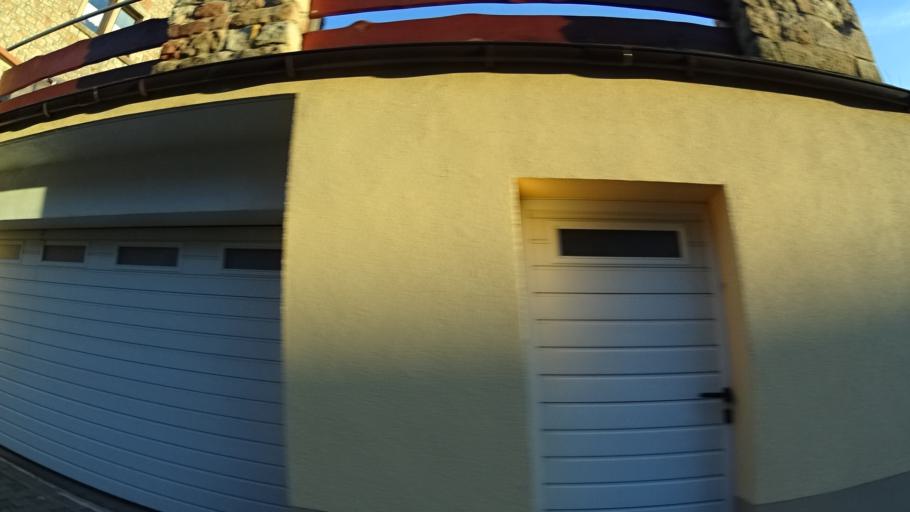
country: DE
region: Rheinland-Pfalz
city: Bolanden
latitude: 49.6394
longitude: 8.0101
